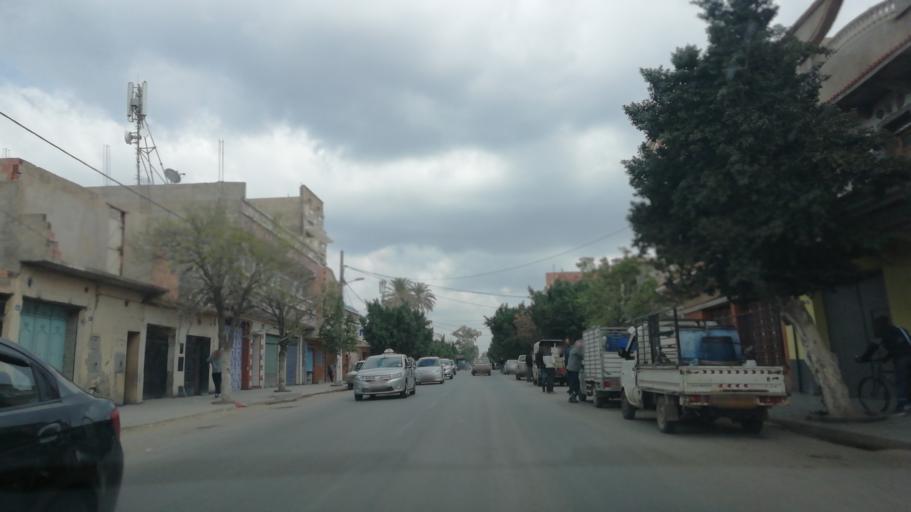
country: DZ
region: Mascara
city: Mascara
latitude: 35.6189
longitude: 0.1110
